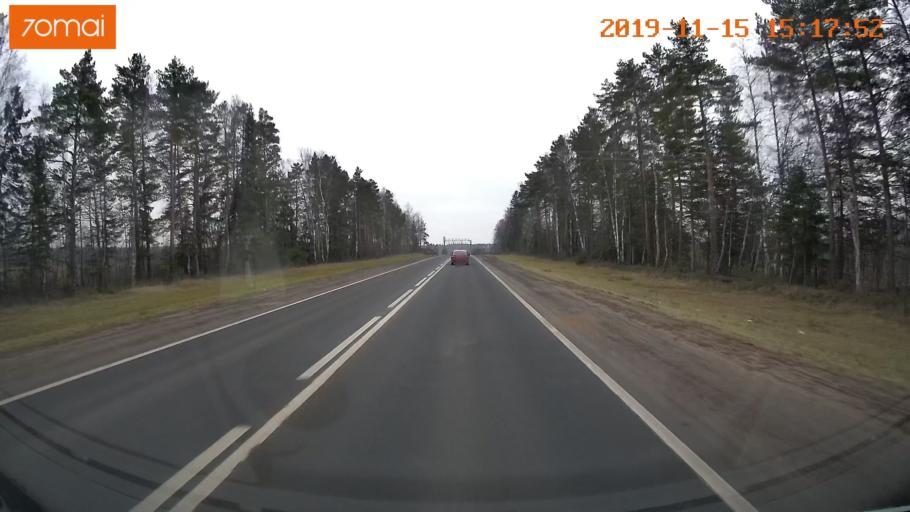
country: RU
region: Jaroslavl
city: Danilov
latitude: 58.2546
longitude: 40.1807
